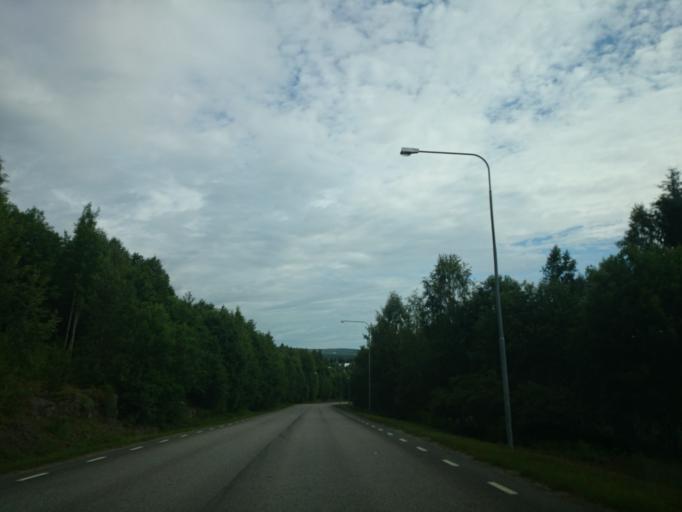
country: SE
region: Vaesternorrland
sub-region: Timra Kommun
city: Timra
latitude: 62.4889
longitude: 17.3197
